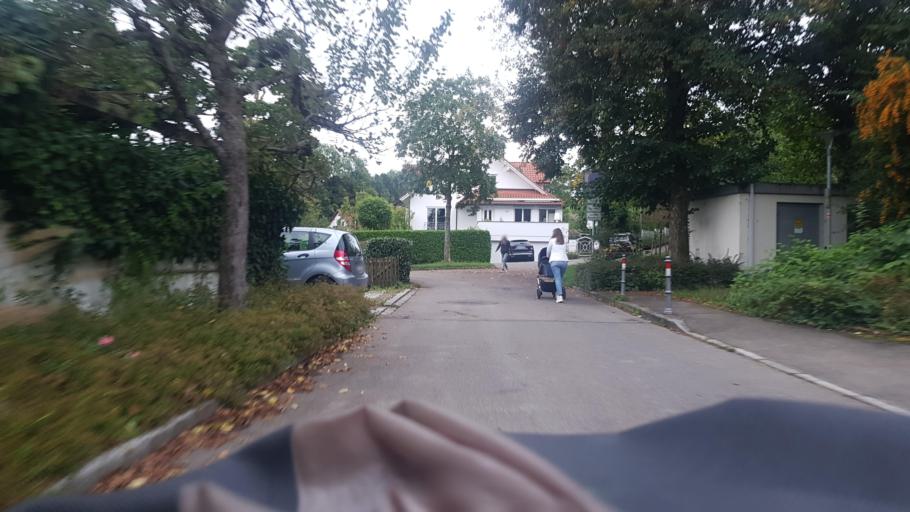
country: DE
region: Bavaria
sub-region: Swabia
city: Bodolz
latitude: 47.5608
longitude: 9.6704
